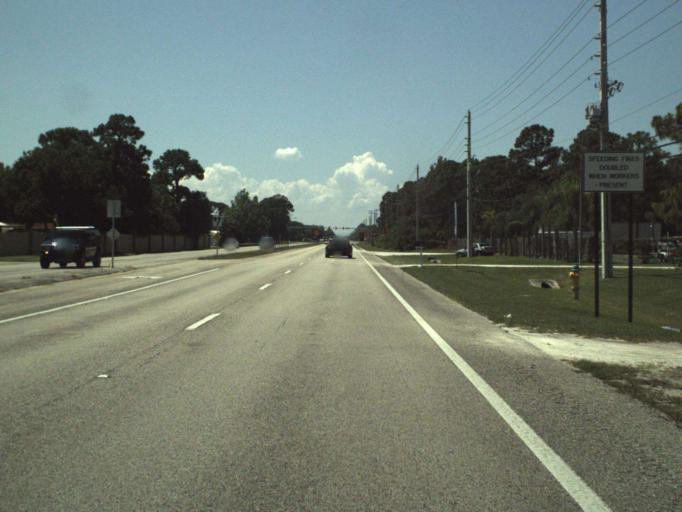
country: US
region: Florida
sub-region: Brevard County
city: Sharpes
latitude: 28.4386
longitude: -80.7087
